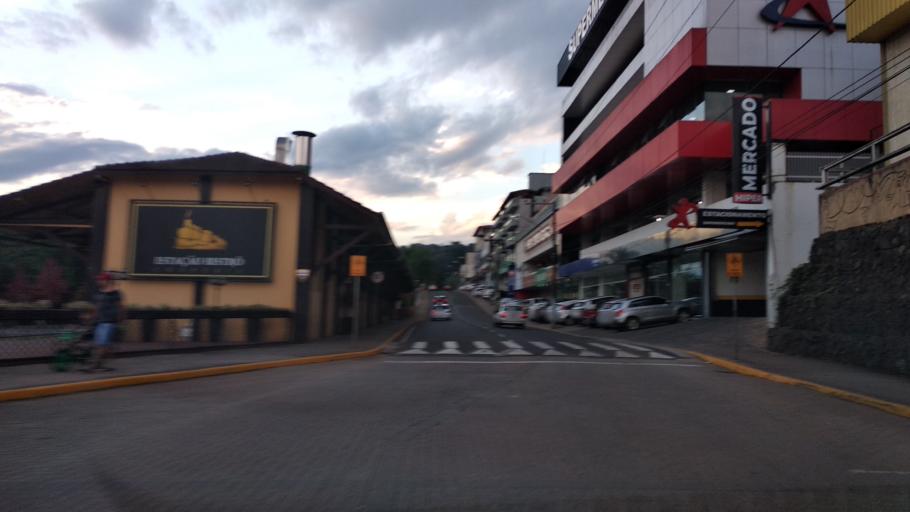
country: BR
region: Santa Catarina
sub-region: Videira
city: Videira
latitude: -27.0044
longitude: -51.1551
